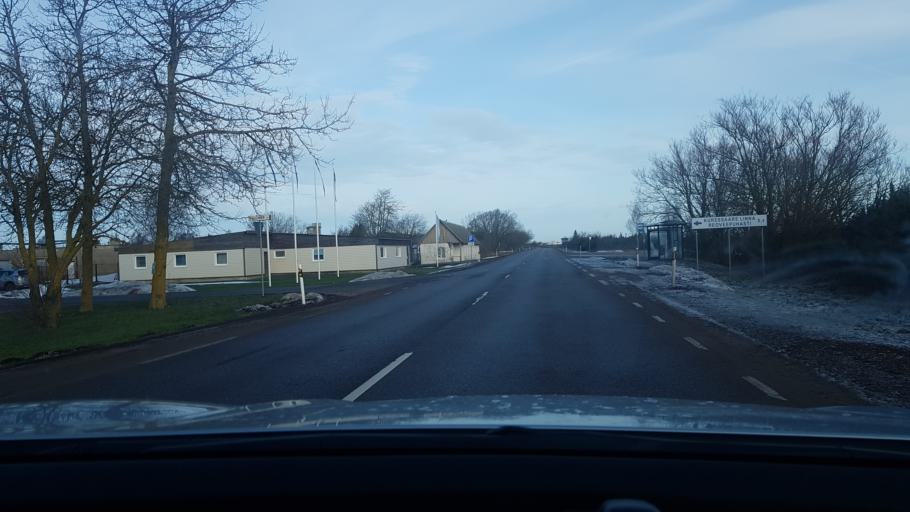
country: EE
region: Saare
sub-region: Kuressaare linn
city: Kuressaare
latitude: 58.2236
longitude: 22.5064
